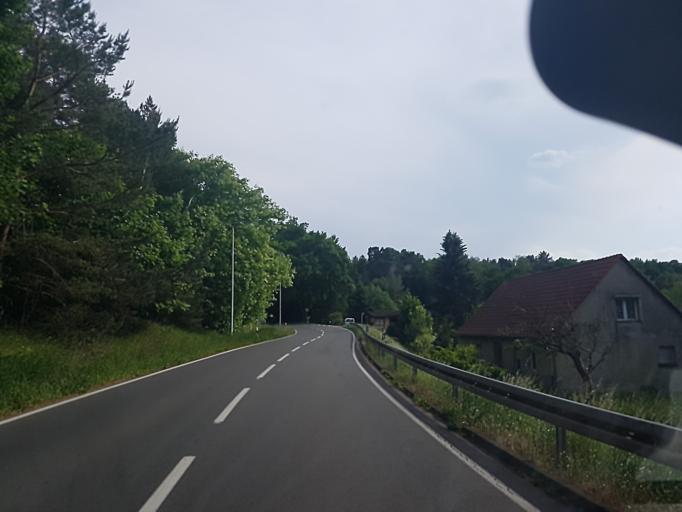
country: DE
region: Saxony-Anhalt
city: Nudersdorf
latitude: 51.9295
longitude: 12.6021
